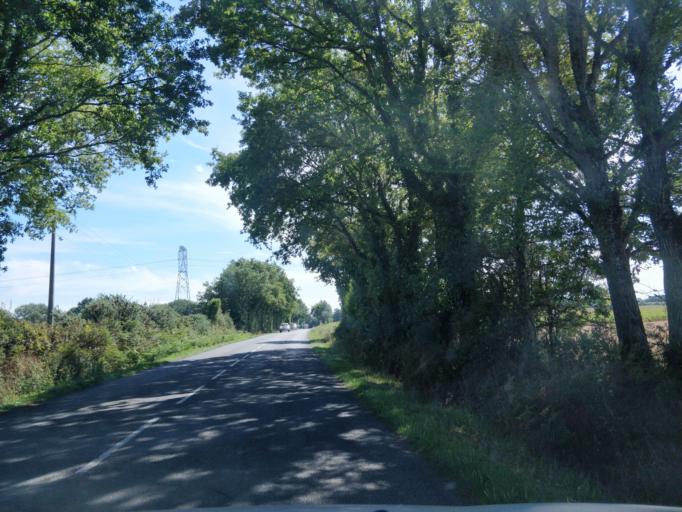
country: FR
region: Pays de la Loire
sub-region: Departement de la Loire-Atlantique
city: Derval
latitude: 47.6879
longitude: -1.6904
